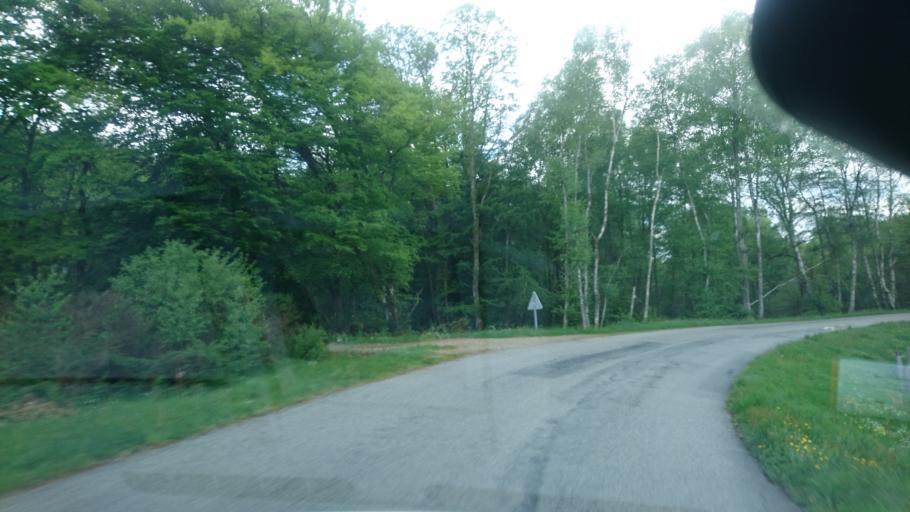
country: FR
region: Limousin
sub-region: Departement de la Haute-Vienne
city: Peyrat-le-Chateau
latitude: 45.7908
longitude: 1.9217
